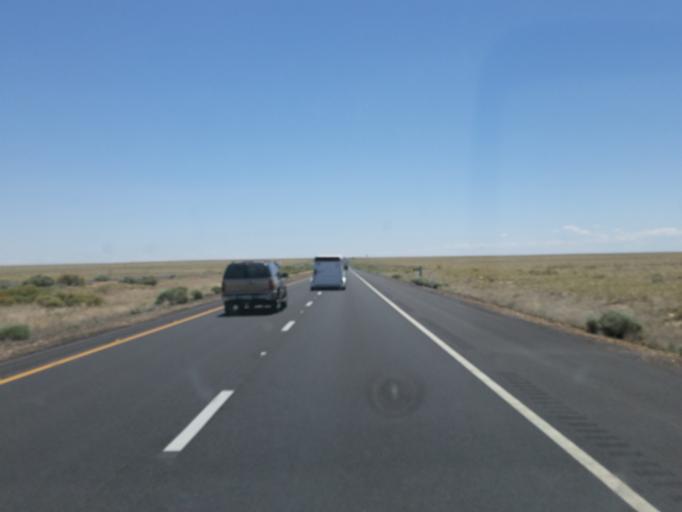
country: US
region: Arizona
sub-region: Coconino County
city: Flagstaff
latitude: 35.1414
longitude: -111.2180
